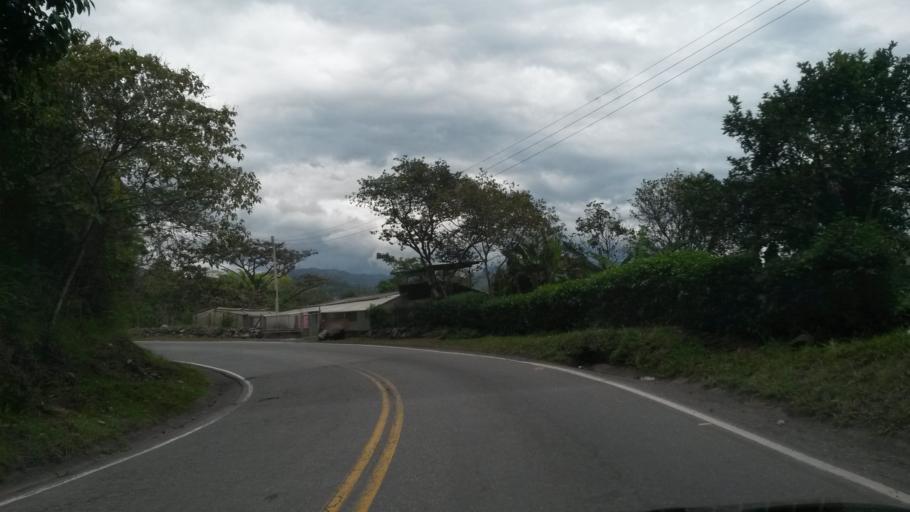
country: CO
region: Cauca
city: Rosas
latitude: 2.2536
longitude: -76.7625
